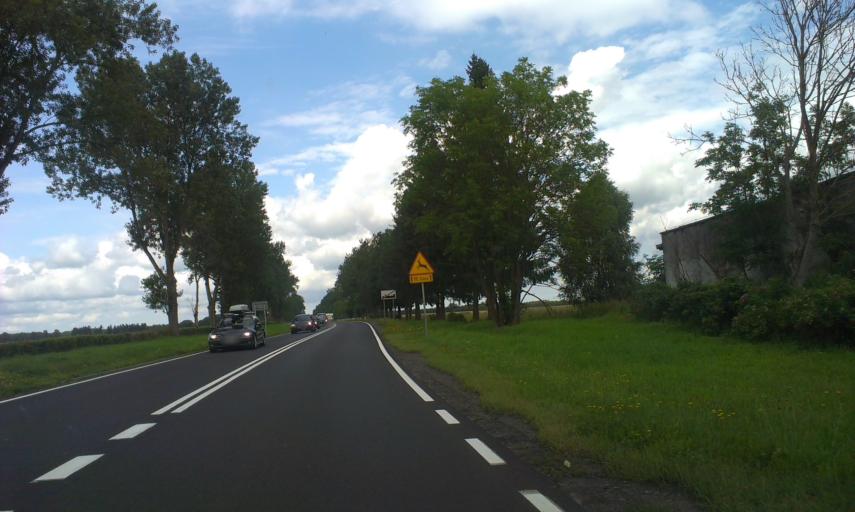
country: PL
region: West Pomeranian Voivodeship
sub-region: Powiat koszalinski
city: Bobolice
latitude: 54.0449
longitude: 16.4407
